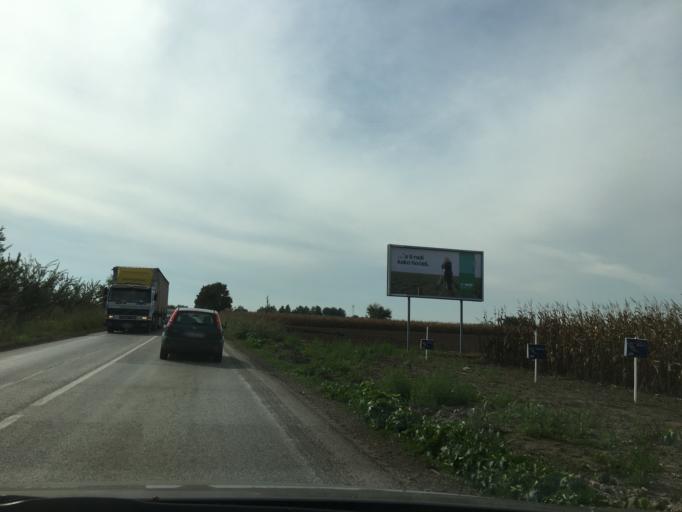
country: RS
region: Autonomna Pokrajina Vojvodina
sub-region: Juznobacki Okrug
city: Temerin
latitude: 45.4535
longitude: 19.9079
